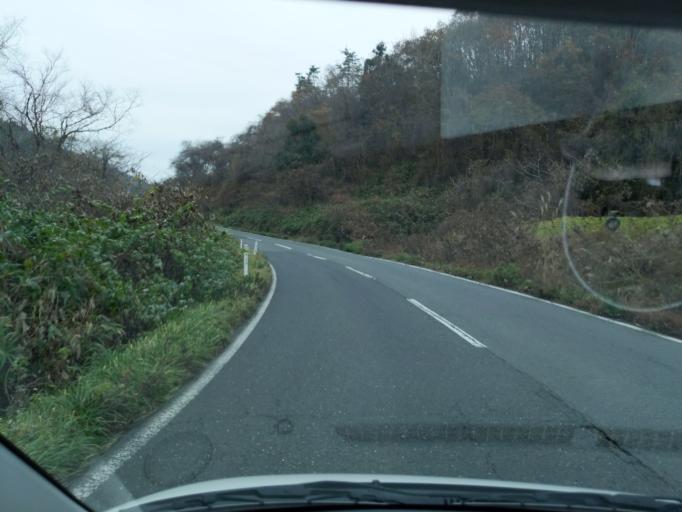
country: JP
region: Iwate
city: Kitakami
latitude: 39.2678
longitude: 141.1810
